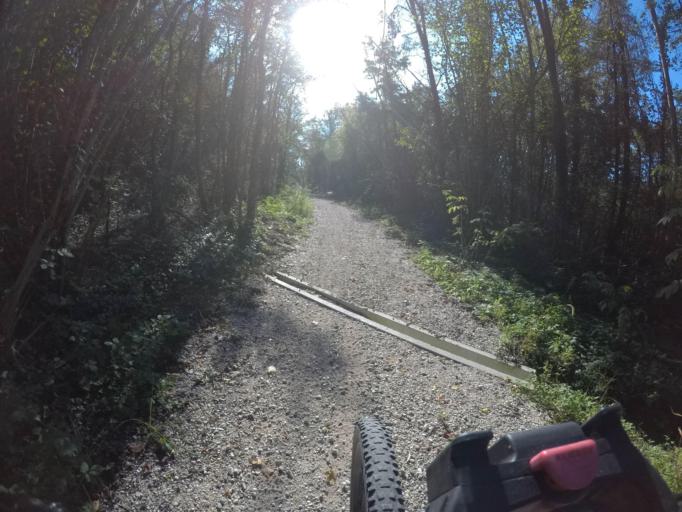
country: IT
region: Friuli Venezia Giulia
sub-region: Provincia di Udine
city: Buttrio
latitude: 46.0154
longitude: 13.3544
